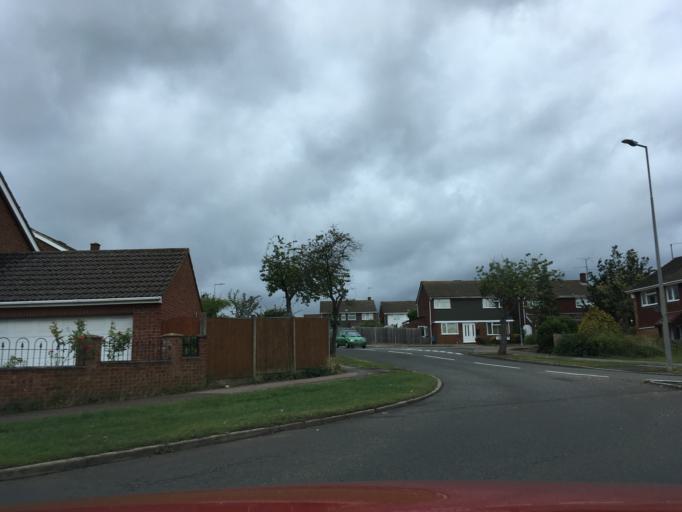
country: GB
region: England
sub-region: Buckinghamshire
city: Bletchley
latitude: 52.0074
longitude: -0.7461
